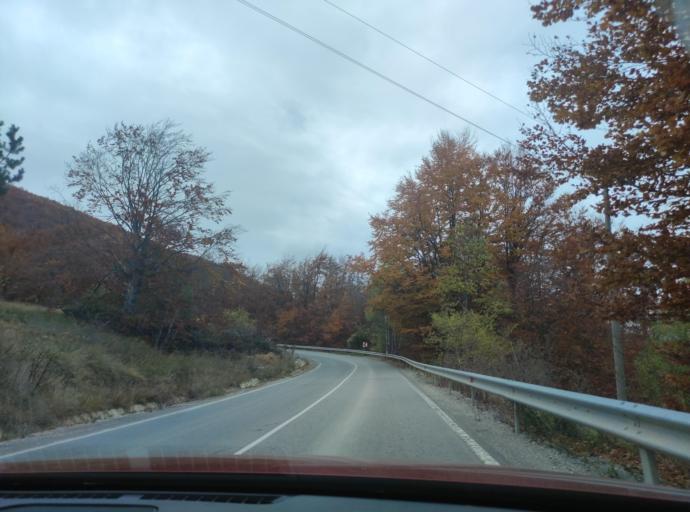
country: BG
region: Sofiya
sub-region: Obshtina Godech
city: Godech
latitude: 43.1077
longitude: 23.1061
